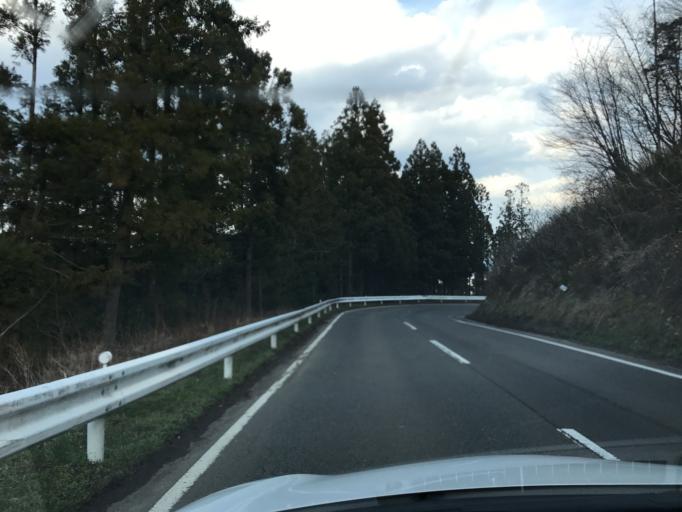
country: JP
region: Miyagi
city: Shiroishi
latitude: 38.0205
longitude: 140.5746
